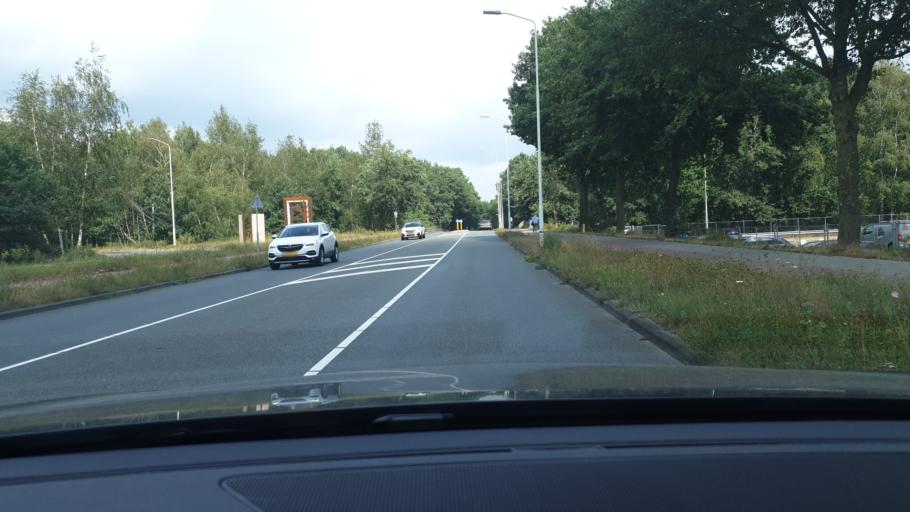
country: NL
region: North Brabant
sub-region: Gemeente Best
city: Best
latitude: 51.4920
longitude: 5.3852
